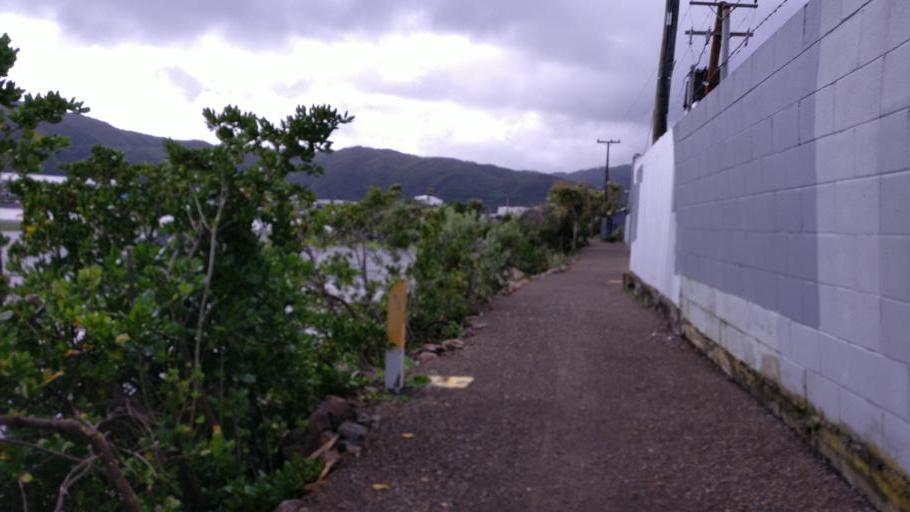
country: NZ
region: Wellington
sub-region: Lower Hutt City
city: Lower Hutt
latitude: -41.2339
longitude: 174.8976
